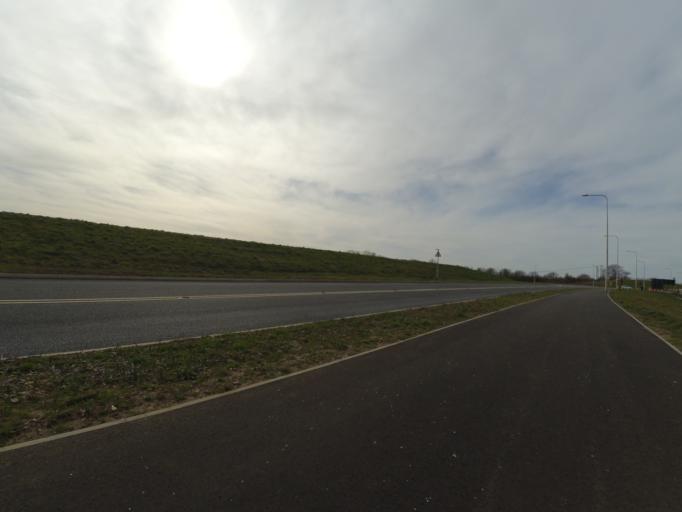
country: GB
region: England
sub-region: Warwickshire
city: Rugby
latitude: 52.3695
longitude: -1.2199
